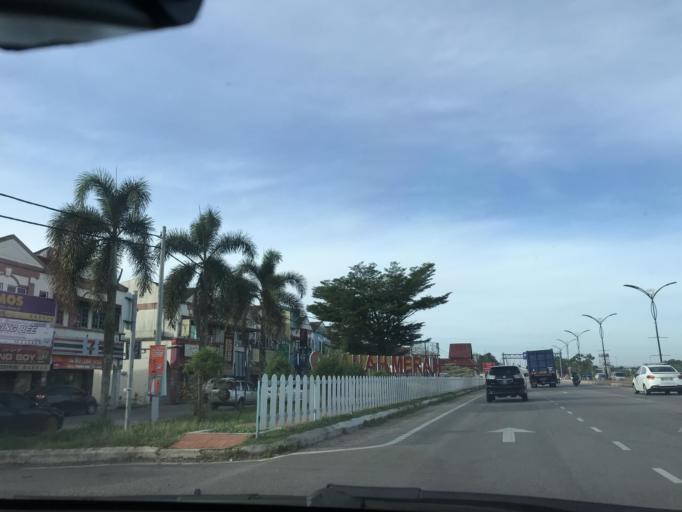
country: MY
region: Kelantan
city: Tanah Merah
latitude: 5.8144
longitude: 102.1482
